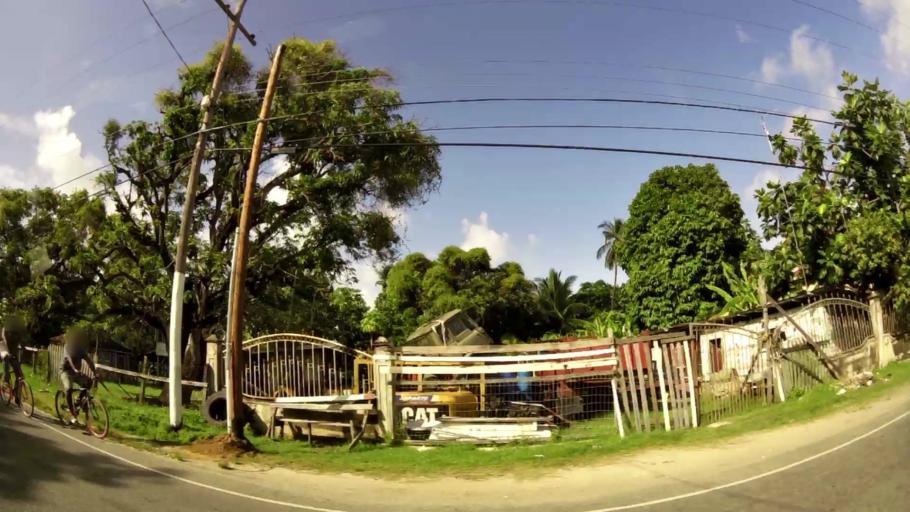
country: GY
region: Demerara-Mahaica
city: Mahaica Village
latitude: 6.7517
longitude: -57.9717
